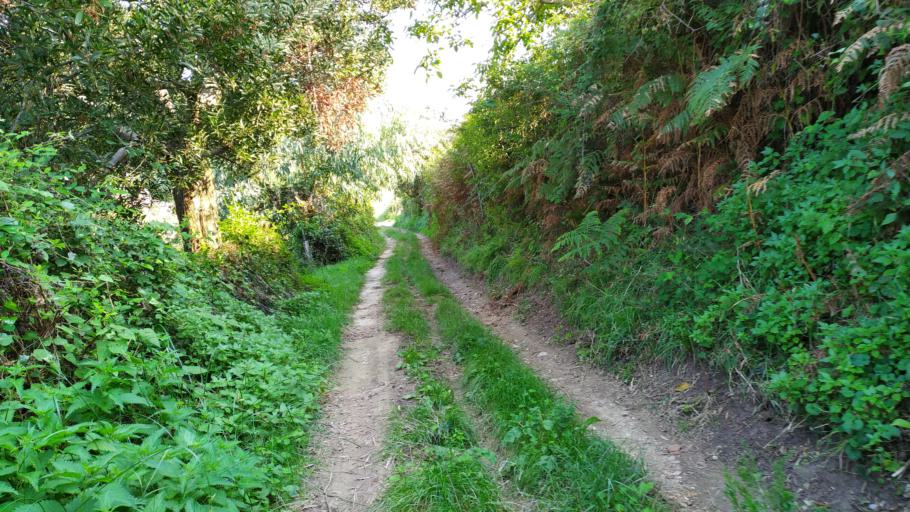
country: IT
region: Sicily
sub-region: Messina
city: Condro
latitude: 38.1616
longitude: 15.3335
